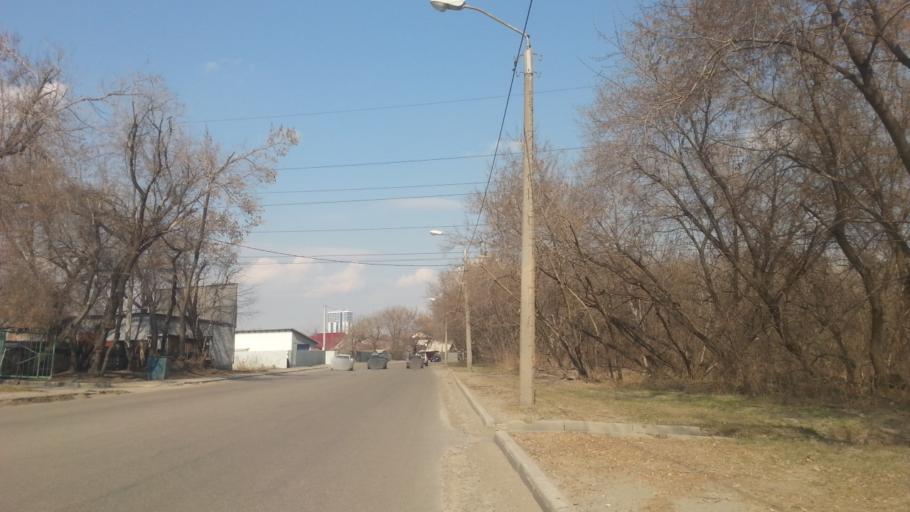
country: RU
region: Altai Krai
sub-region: Gorod Barnaulskiy
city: Barnaul
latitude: 53.3209
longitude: 83.7636
